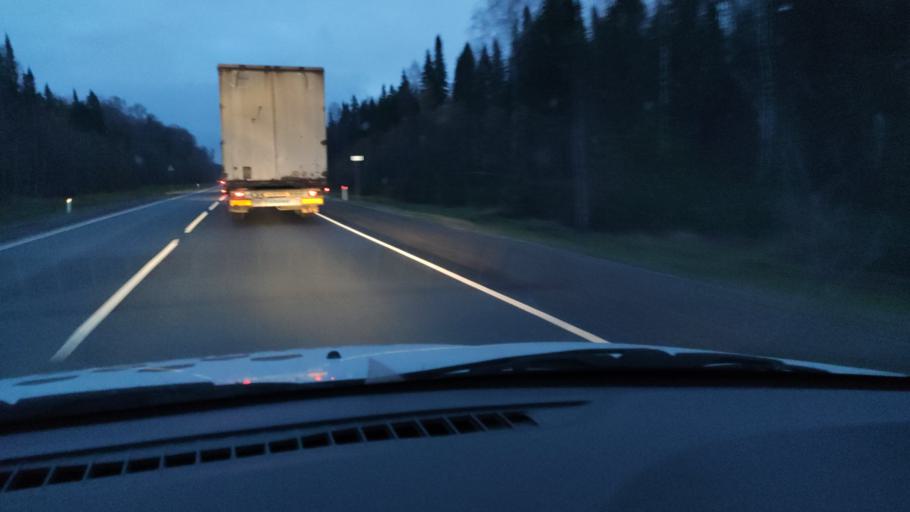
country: RU
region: Kirov
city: Kostino
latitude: 58.8335
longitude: 53.4760
